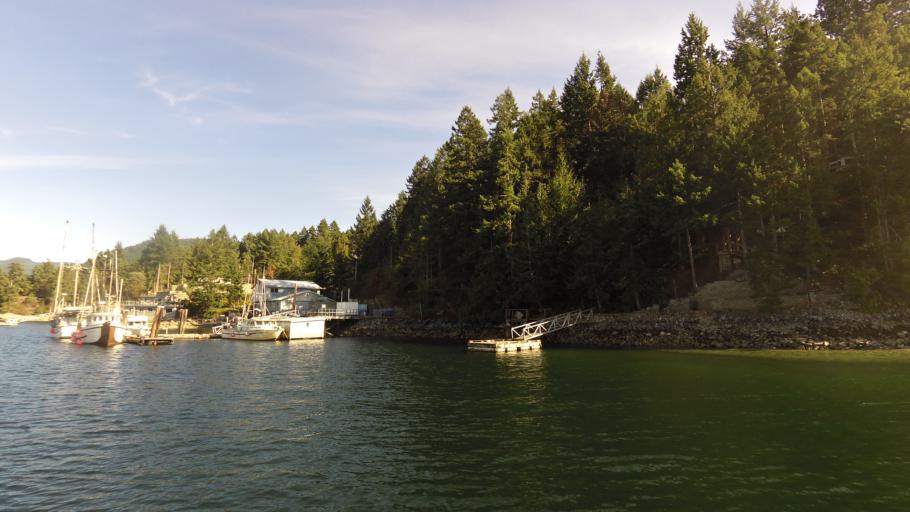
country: CA
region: British Columbia
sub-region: Sunshine Coast Regional District
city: Sechelt
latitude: 49.6272
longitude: -124.0436
